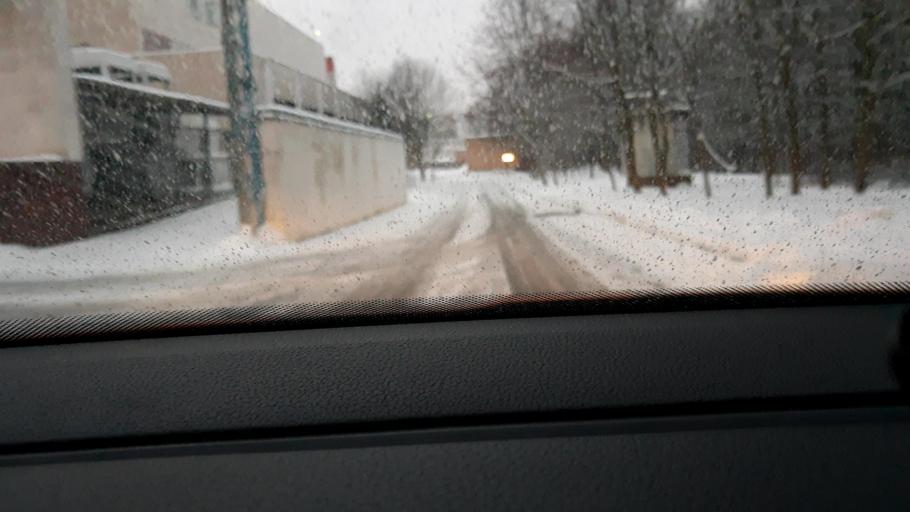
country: RU
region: Moscow
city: Rublevo
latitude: 55.7566
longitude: 37.3808
